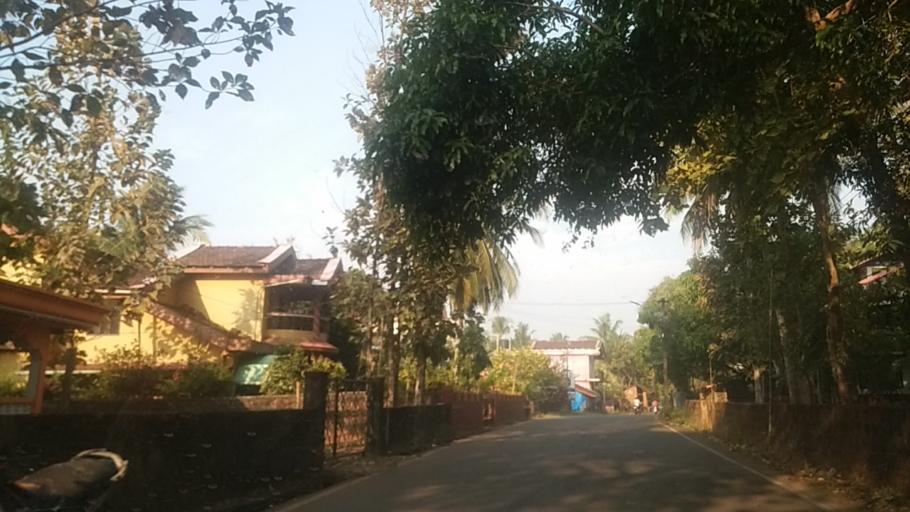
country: IN
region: Goa
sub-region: South Goa
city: Chinchinim
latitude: 15.2355
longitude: 73.9844
